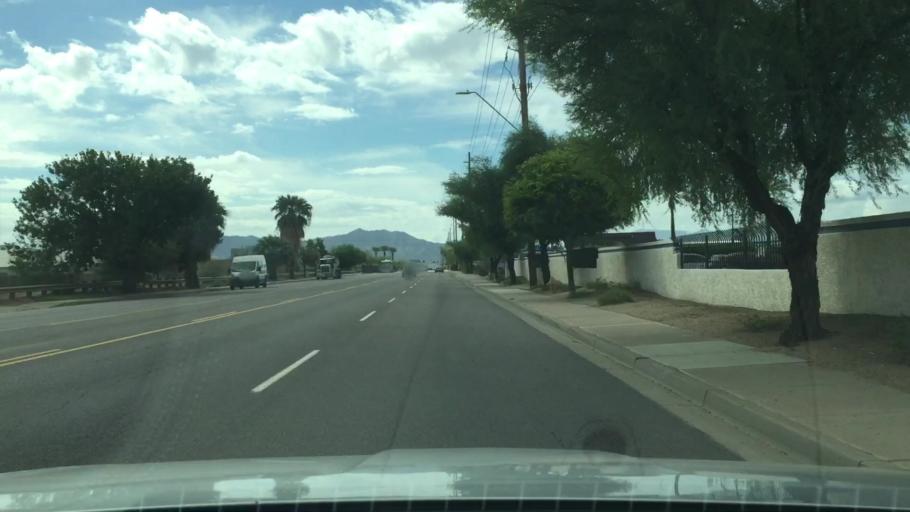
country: US
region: Arizona
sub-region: Maricopa County
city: Phoenix
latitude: 33.4285
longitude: -112.1346
